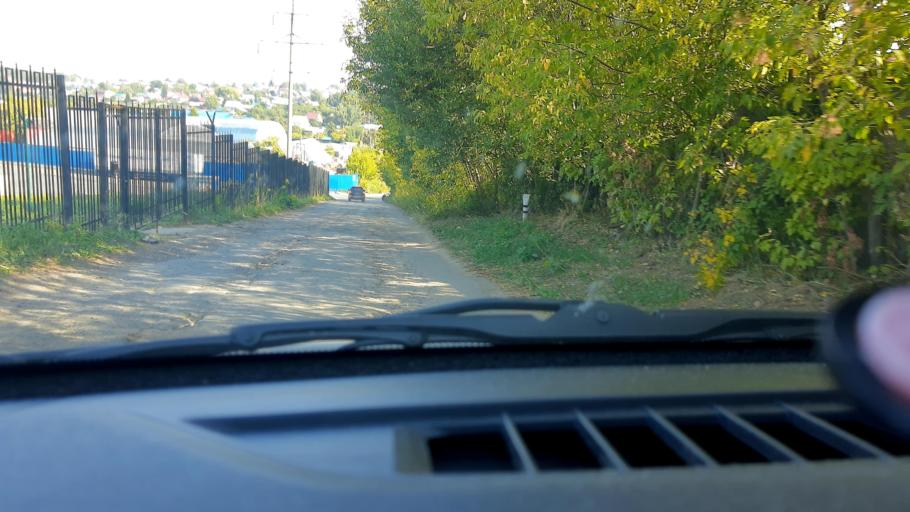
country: RU
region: Nizjnij Novgorod
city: Nizhniy Novgorod
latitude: 56.2447
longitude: 43.9943
